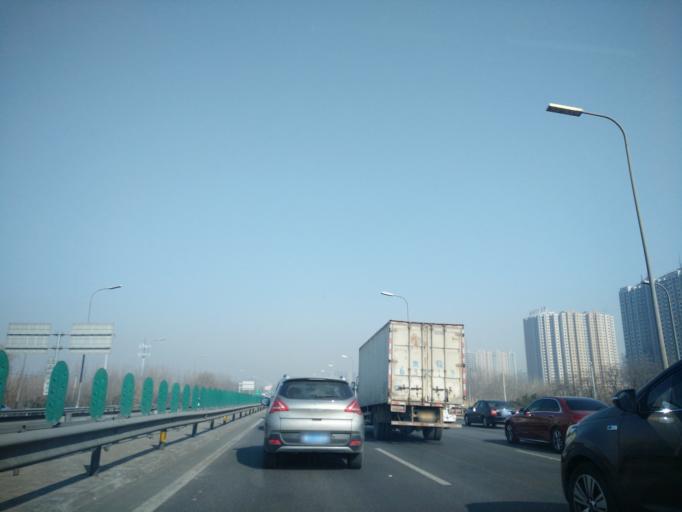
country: CN
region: Beijing
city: Dongba
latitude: 39.9593
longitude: 116.5226
